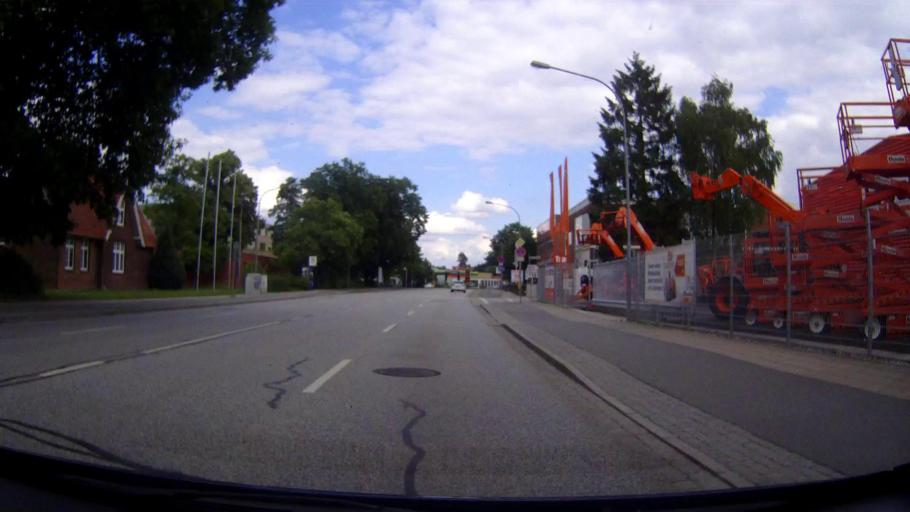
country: DE
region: Schleswig-Holstein
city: Luebeck
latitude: 53.8478
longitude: 10.6722
